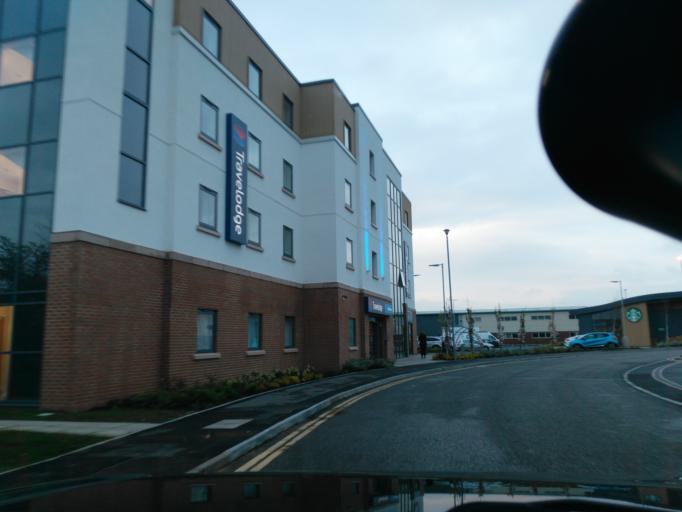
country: GB
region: England
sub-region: Wiltshire
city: Melksham
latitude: 51.3547
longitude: -2.1403
